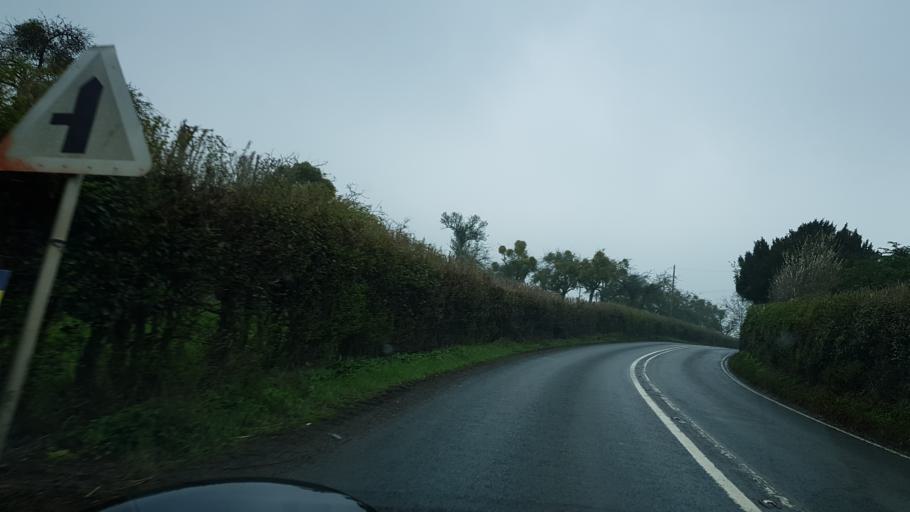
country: GB
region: England
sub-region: Herefordshire
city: Yatton
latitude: 52.0004
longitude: -2.4981
